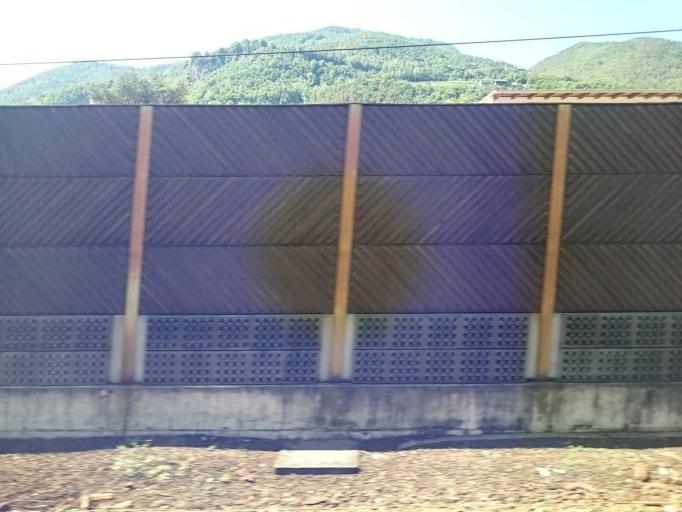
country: IT
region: Trentino-Alto Adige
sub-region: Bolzano
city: Cardano
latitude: 46.4949
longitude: 11.3917
